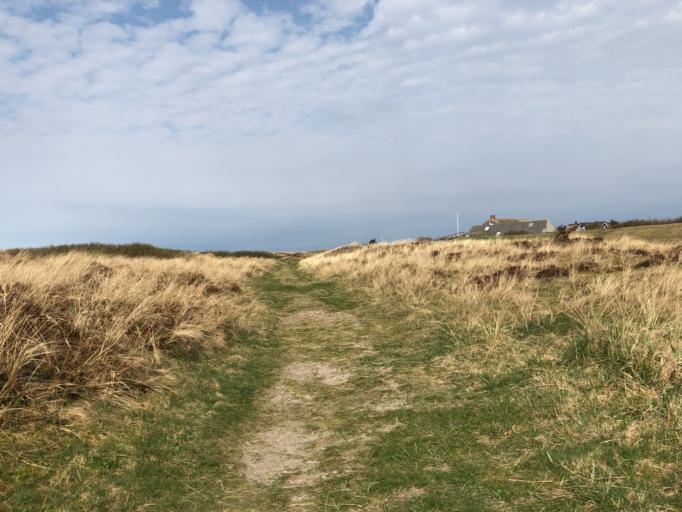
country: DK
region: South Denmark
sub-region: Varde Kommune
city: Oksbol
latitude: 55.5444
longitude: 8.1312
